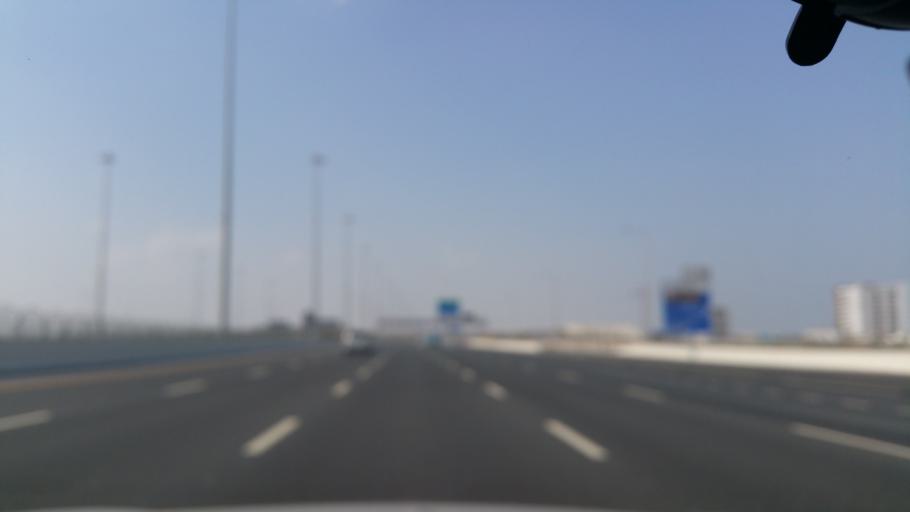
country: QA
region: Baladiyat Umm Salal
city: Umm Salal Muhammad
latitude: 25.4222
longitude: 51.4865
